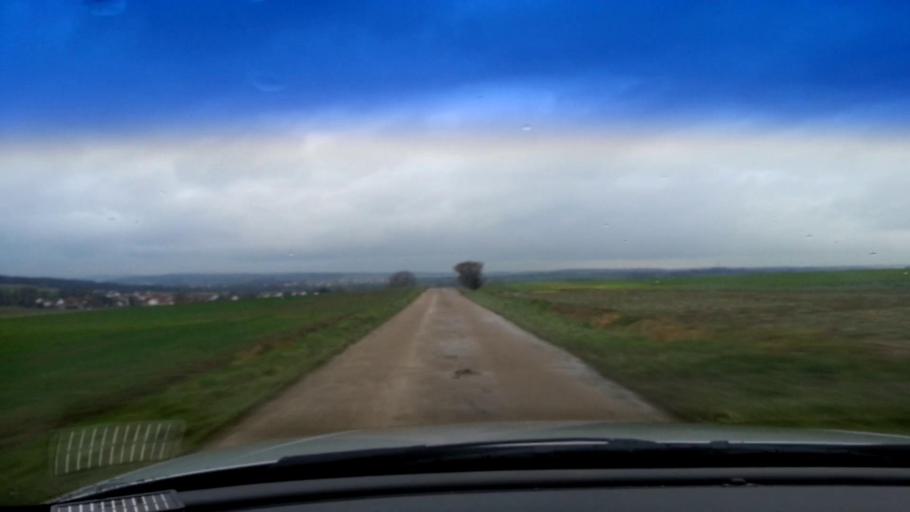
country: DE
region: Bavaria
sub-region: Upper Franconia
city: Litzendorf
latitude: 49.9408
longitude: 11.0091
